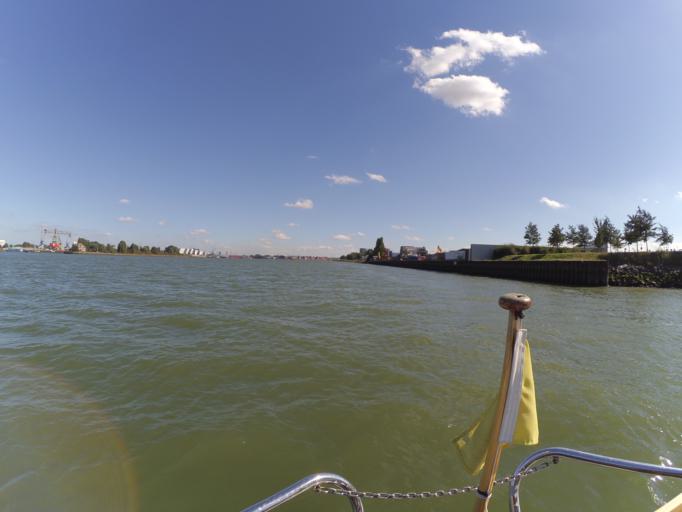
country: NL
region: South Holland
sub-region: Gemeente Schiedam
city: Schiedam
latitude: 51.8968
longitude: 4.3748
